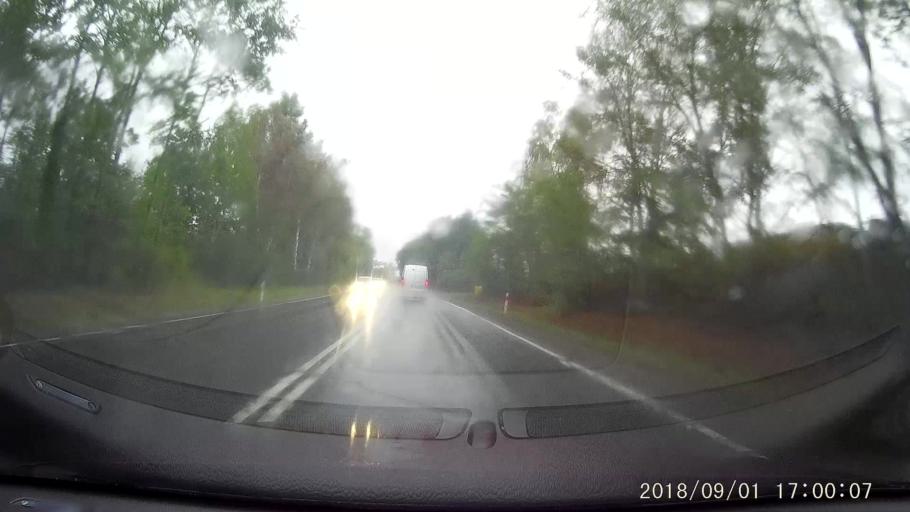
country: PL
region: Lubusz
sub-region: Powiat zielonogorski
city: Swidnica
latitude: 51.9012
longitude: 15.4070
